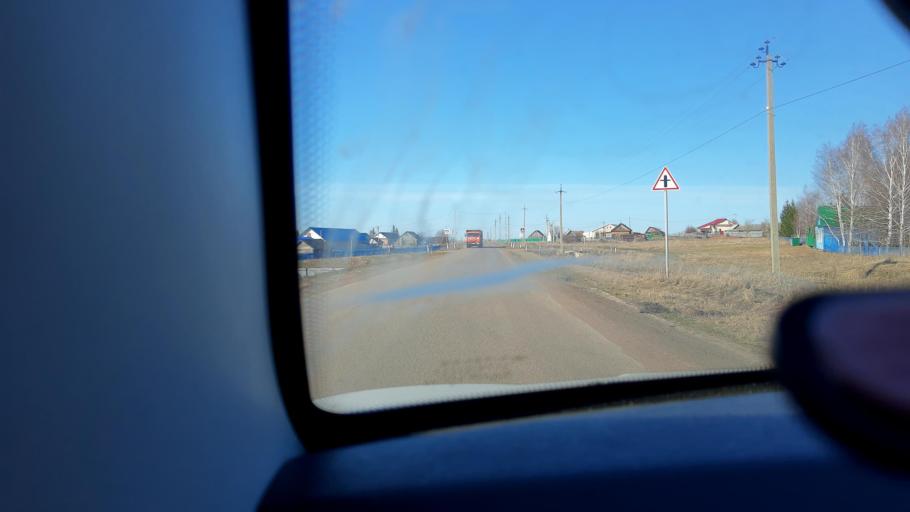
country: RU
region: Bashkortostan
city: Asanovo
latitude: 54.8411
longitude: 55.4577
